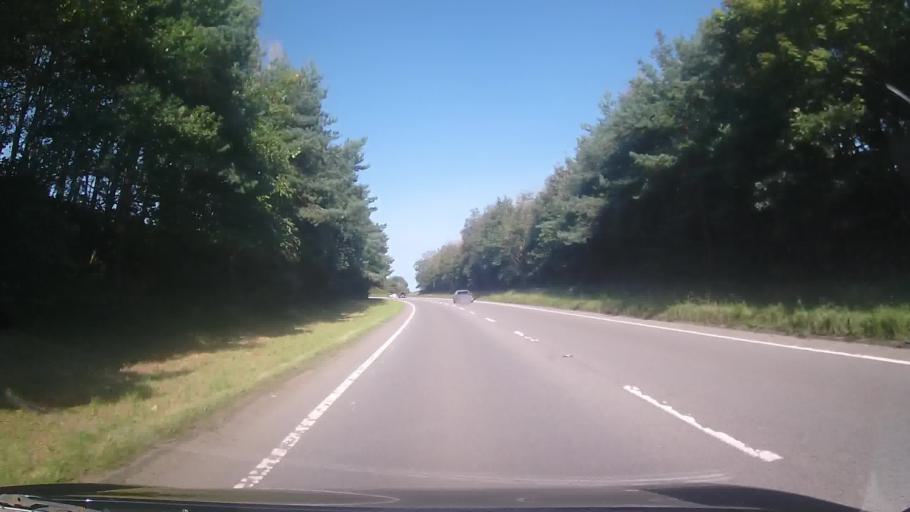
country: GB
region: Wales
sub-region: Pembrokeshire
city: Haverfordwest
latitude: 51.8103
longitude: -4.9558
